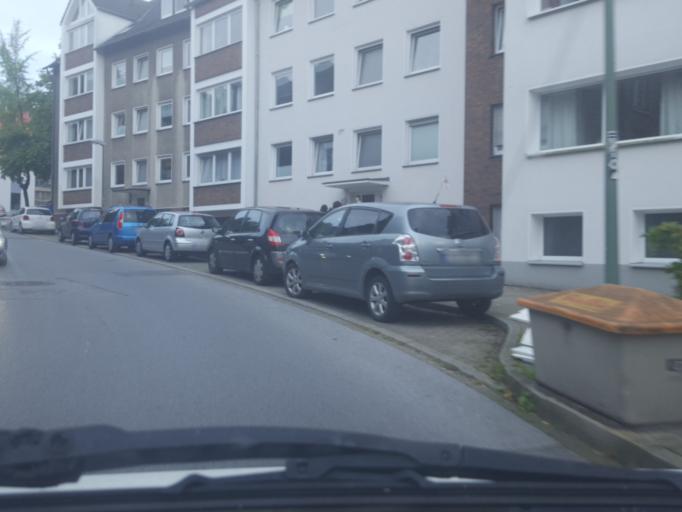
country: DE
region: North Rhine-Westphalia
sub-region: Regierungsbezirk Dusseldorf
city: Velbert
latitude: 51.3869
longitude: 7.0043
